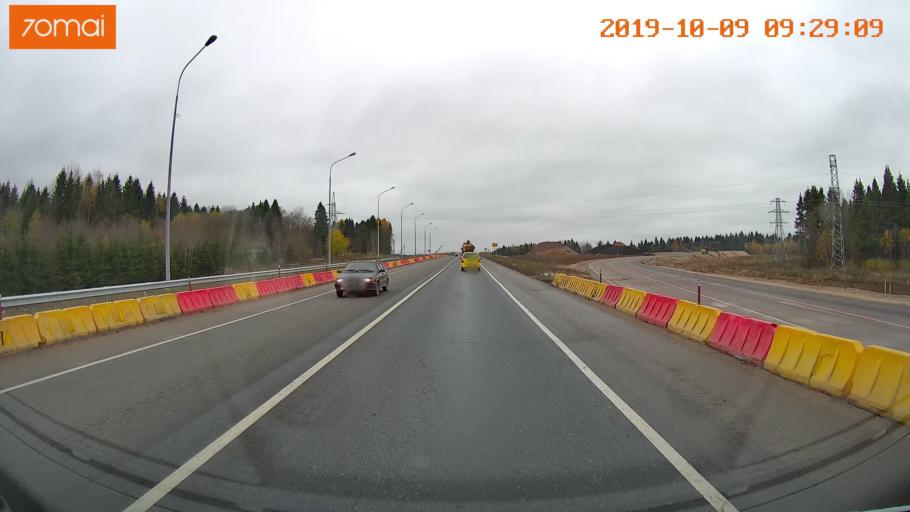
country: RU
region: Vologda
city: Vologda
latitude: 59.1294
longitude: 39.9606
